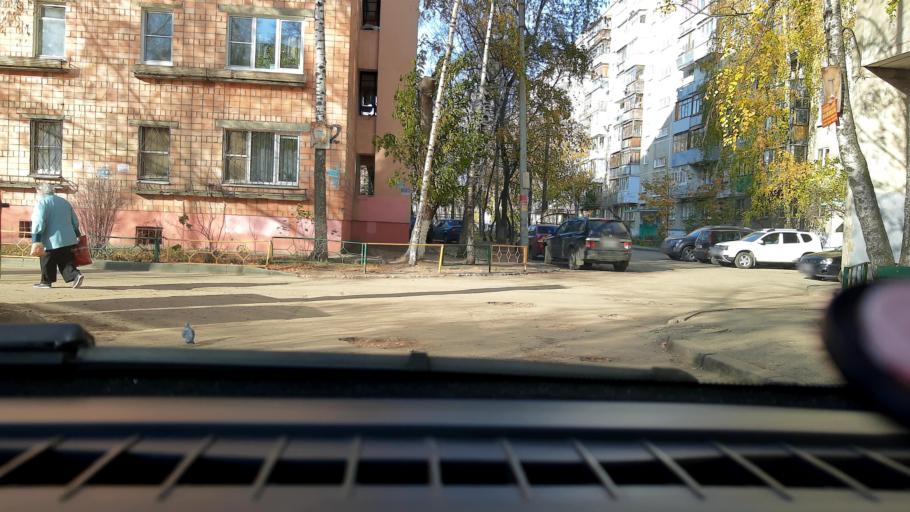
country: RU
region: Nizjnij Novgorod
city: Gorbatovka
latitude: 56.3607
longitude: 43.8192
